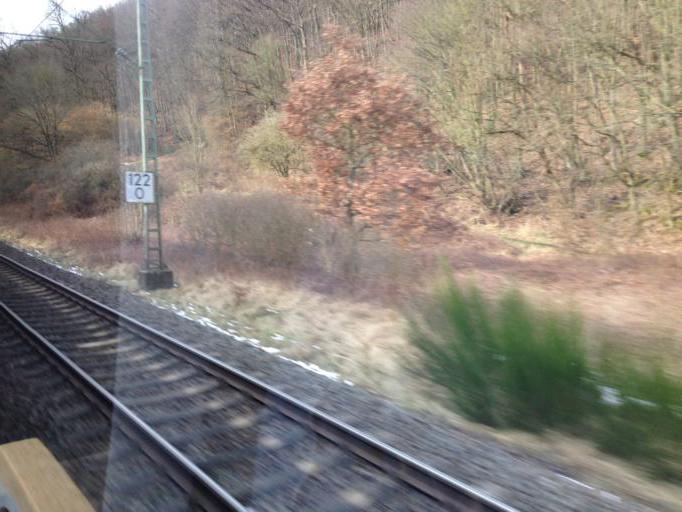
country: DE
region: Hesse
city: Dillenburg
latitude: 50.7478
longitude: 8.2600
